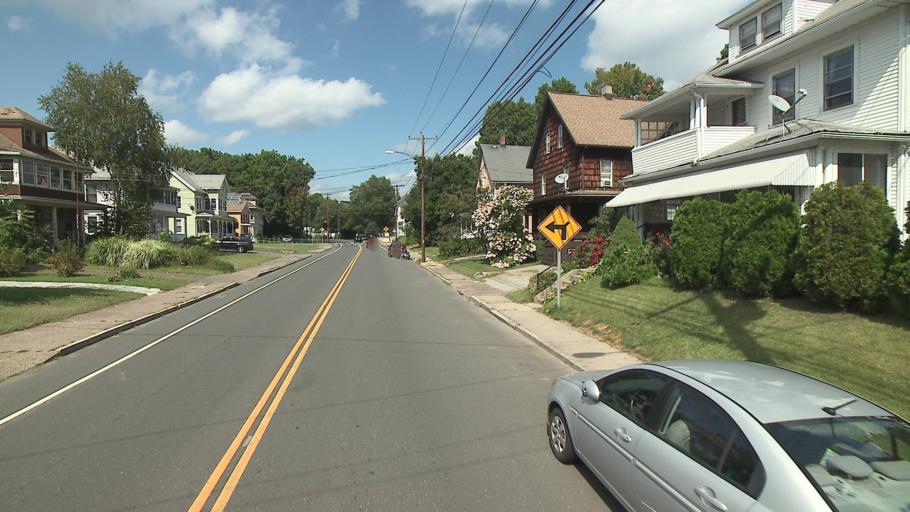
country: US
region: Connecticut
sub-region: New Haven County
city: Ansonia
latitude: 41.3568
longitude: -73.0810
